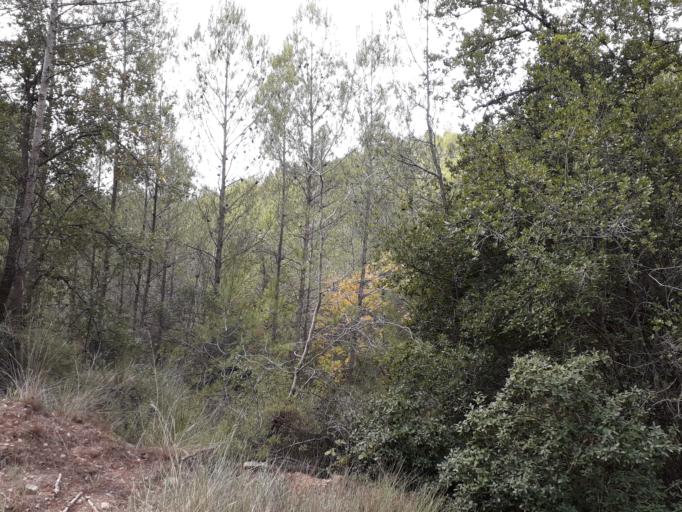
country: ES
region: Catalonia
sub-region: Provincia de Barcelona
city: Jorba
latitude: 41.6088
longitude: 1.4793
